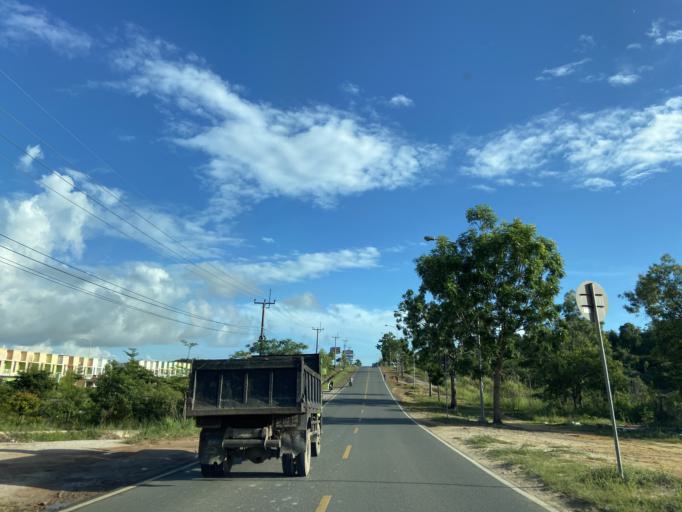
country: SG
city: Singapore
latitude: 1.0073
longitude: 104.0229
